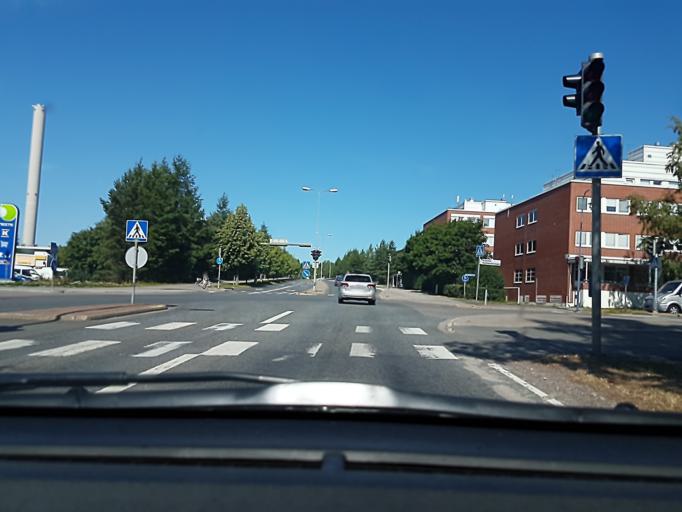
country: FI
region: Uusimaa
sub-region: Helsinki
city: Vantaa
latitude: 60.3187
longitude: 25.0614
